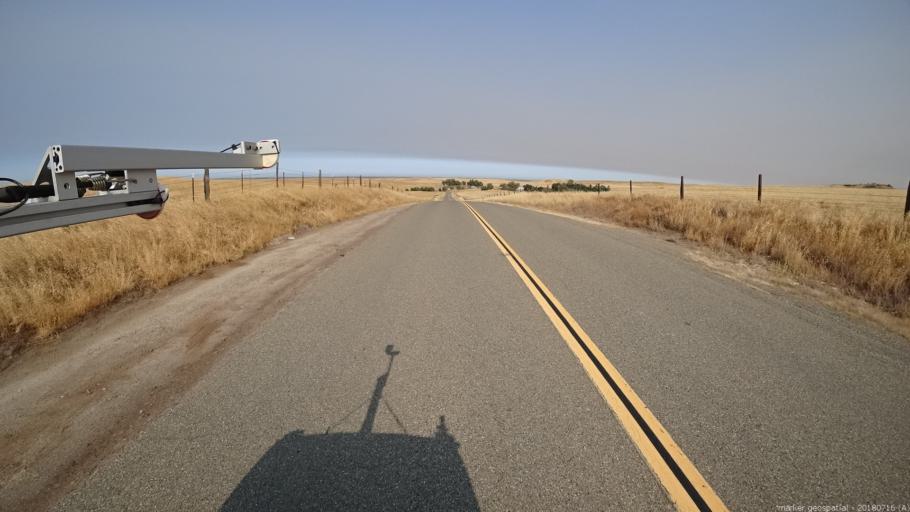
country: US
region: California
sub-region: Madera County
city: Madera Acres
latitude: 37.1193
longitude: -119.9740
